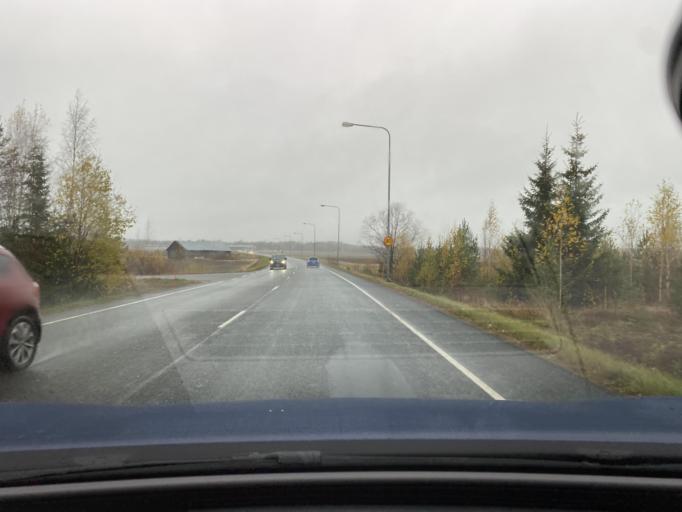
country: FI
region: Varsinais-Suomi
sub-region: Loimaa
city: Loimaa
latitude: 60.8648
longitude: 23.0183
